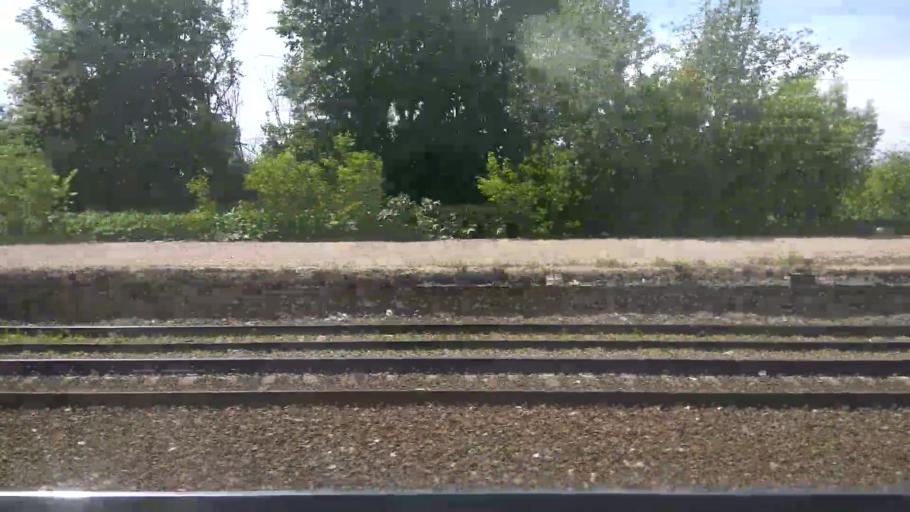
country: RU
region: Moskovskaya
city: Malyshevo
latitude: 55.5015
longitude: 38.3584
